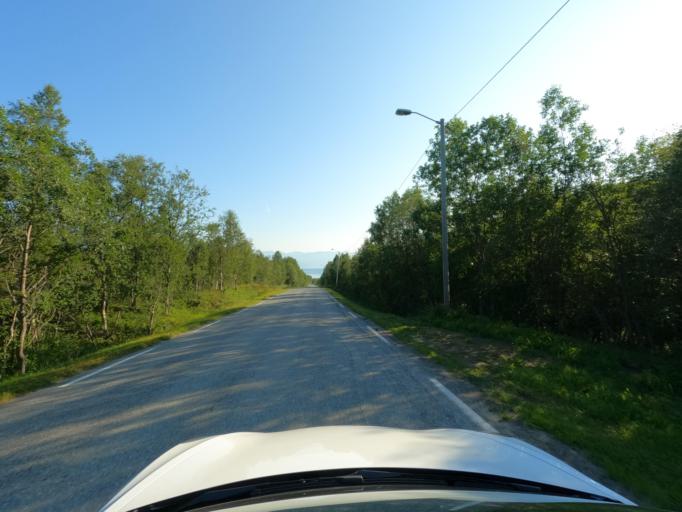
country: NO
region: Nordland
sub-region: Narvik
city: Bjerkvik
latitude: 68.5401
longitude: 17.4896
